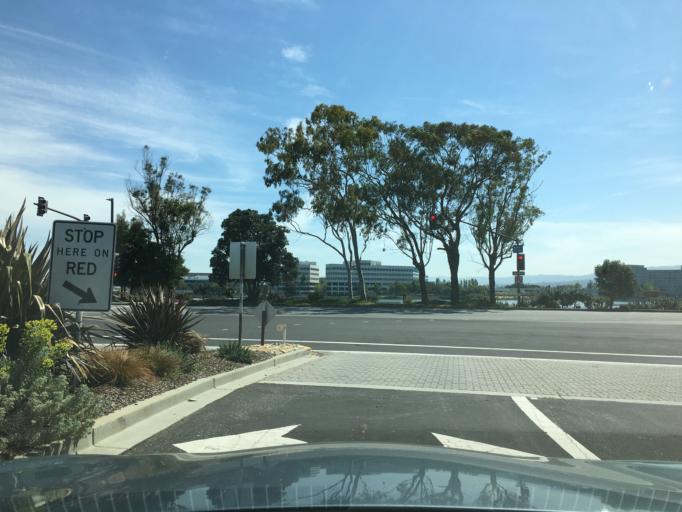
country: US
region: California
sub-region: San Mateo County
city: Redwood Shores
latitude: 37.5291
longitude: -122.2602
